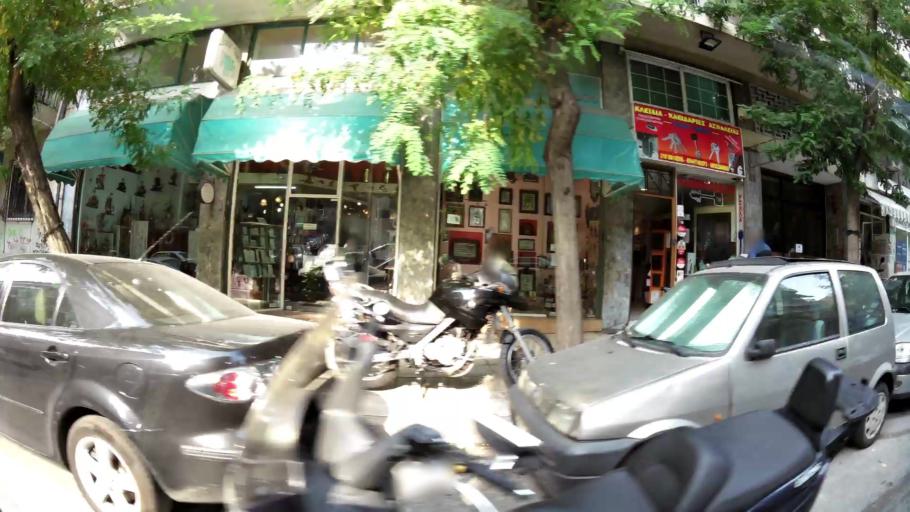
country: GR
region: Attica
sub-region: Nomarchia Athinas
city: Kipseli
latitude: 37.9988
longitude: 23.7415
